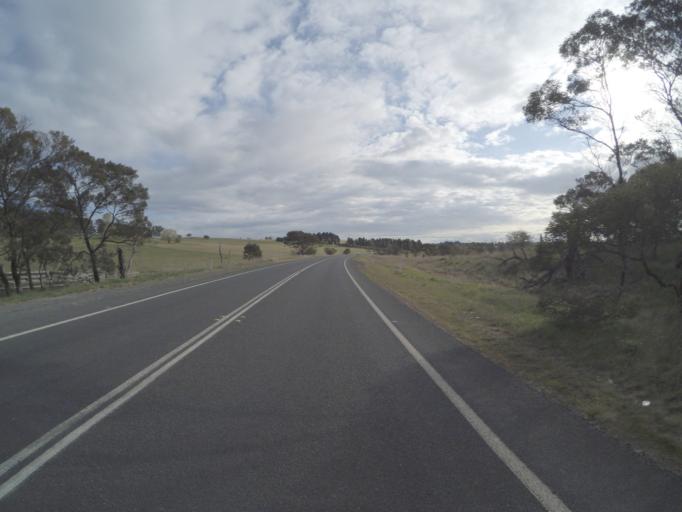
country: AU
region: New South Wales
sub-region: Wingecarribee
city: Bundanoon
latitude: -34.5857
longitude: 150.2957
